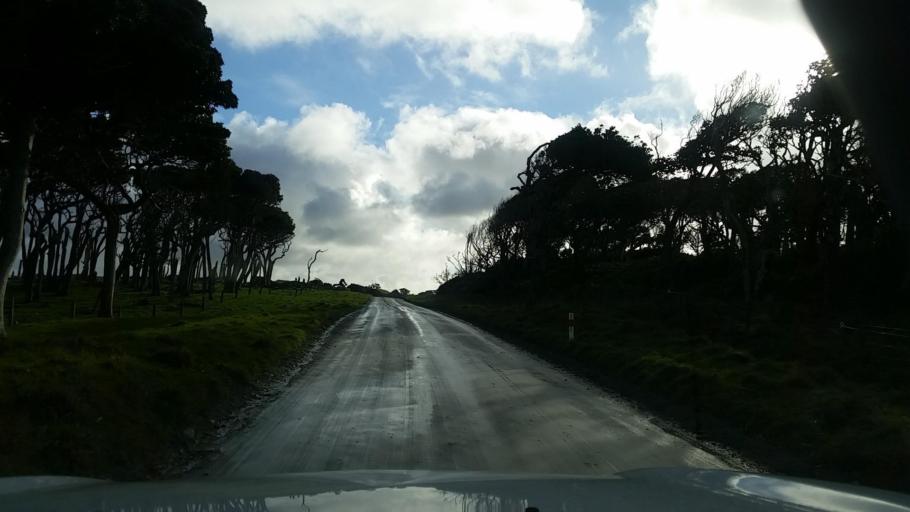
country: NZ
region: Chatham Islands
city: Waitangi
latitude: -43.8212
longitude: -176.5700
